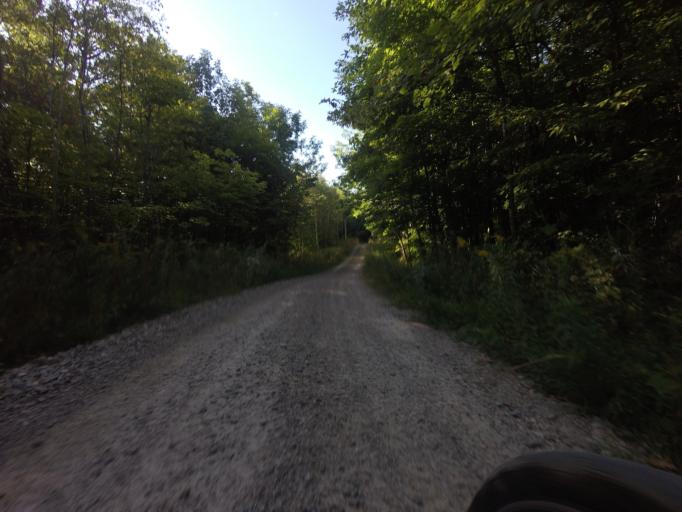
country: CA
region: Ontario
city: Arnprior
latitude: 45.1965
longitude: -76.5221
